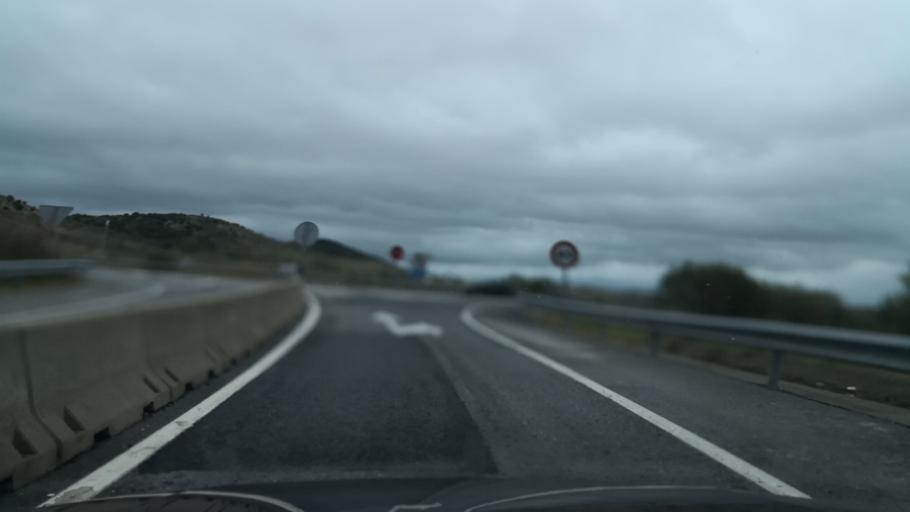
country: ES
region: Extremadura
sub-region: Provincia de Caceres
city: Caceres
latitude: 39.4306
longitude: -6.4078
